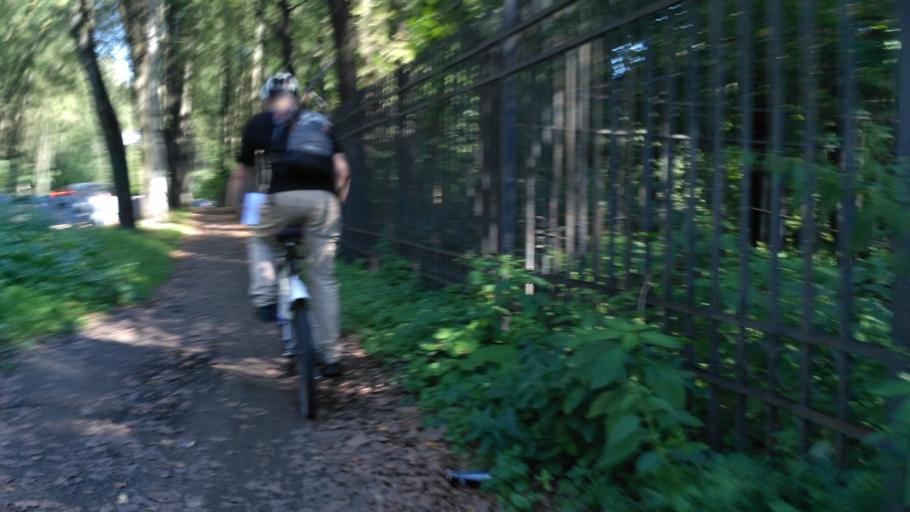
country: RU
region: Moskovskaya
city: Izmaylovo
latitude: 55.7769
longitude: 37.7631
